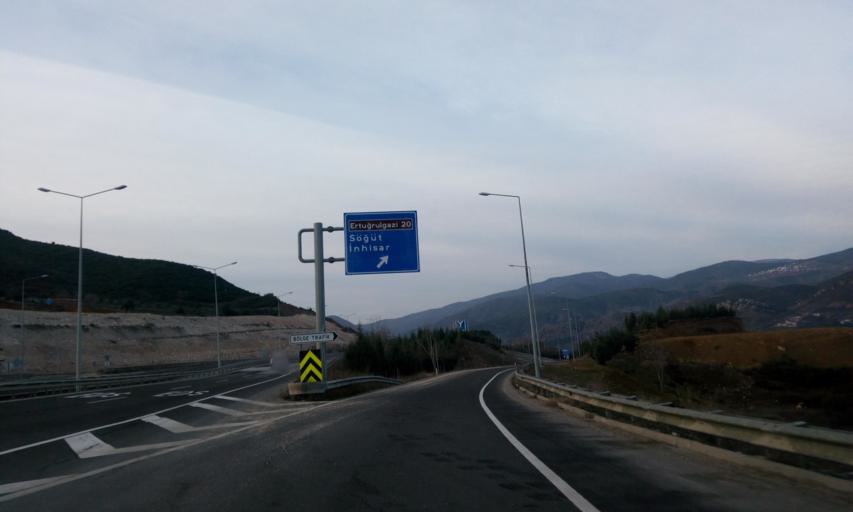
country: TR
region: Bilecik
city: Kuplu
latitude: 40.1225
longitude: 30.0131
